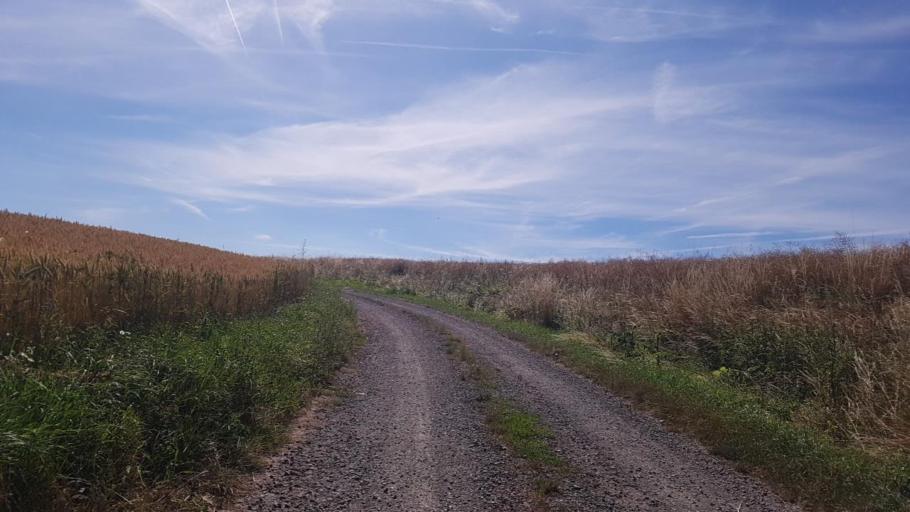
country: DE
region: North Rhine-Westphalia
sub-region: Regierungsbezirk Koln
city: Kall
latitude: 50.6177
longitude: 6.5576
